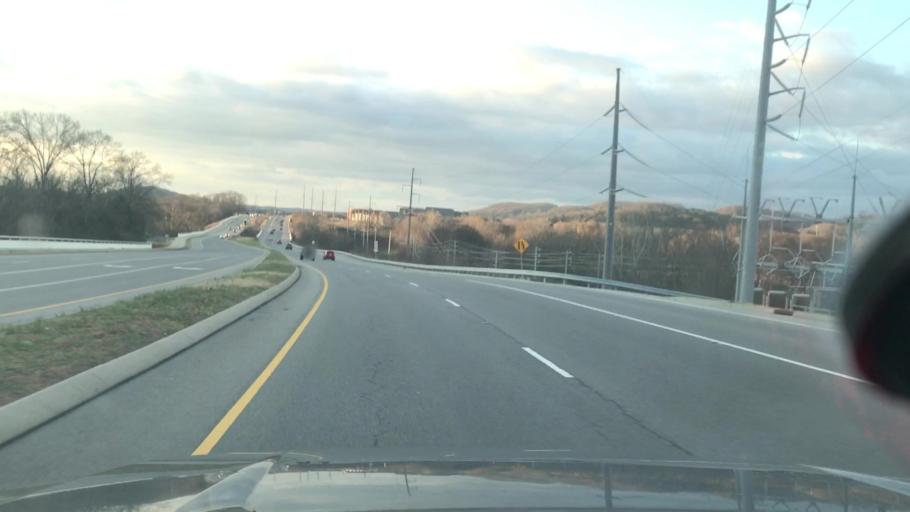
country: US
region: Tennessee
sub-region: Williamson County
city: Franklin
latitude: 35.9415
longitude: -86.8403
